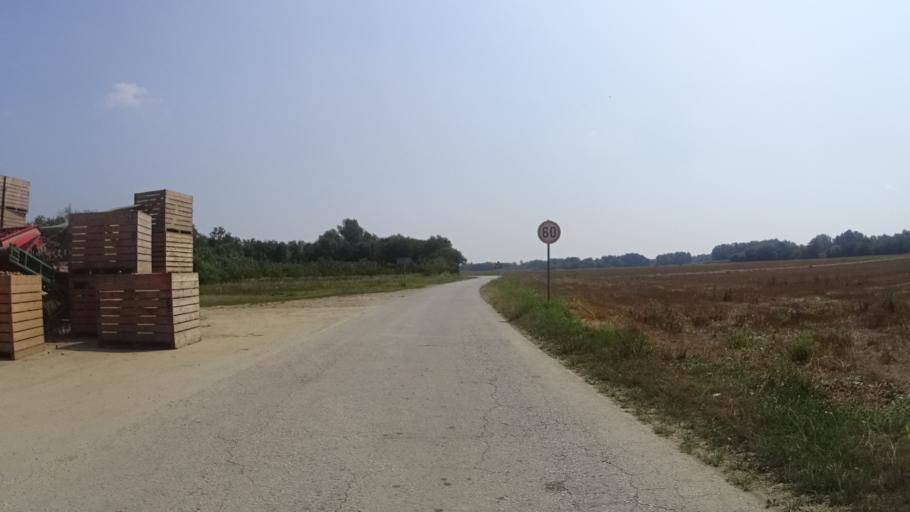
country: HR
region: Medimurska
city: Domasinec
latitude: 46.3939
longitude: 16.6015
